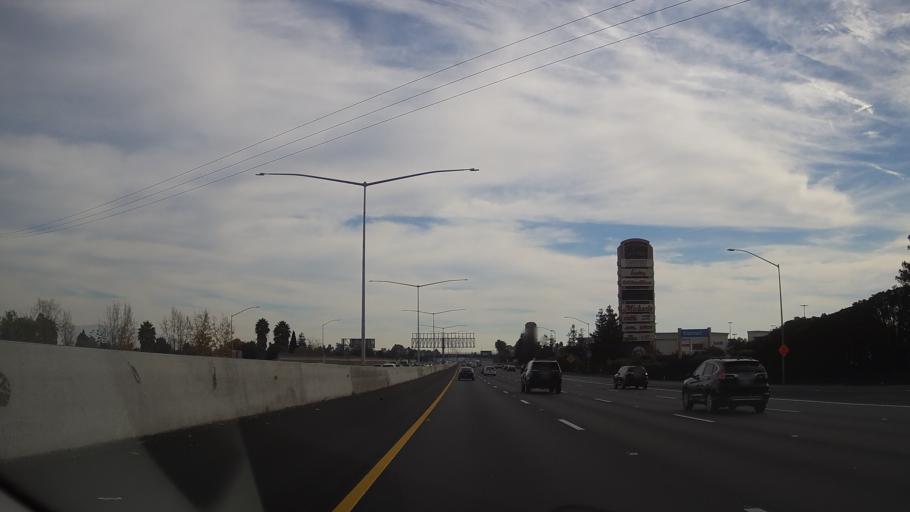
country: US
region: California
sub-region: Alameda County
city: Union City
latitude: 37.6055
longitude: -122.0658
